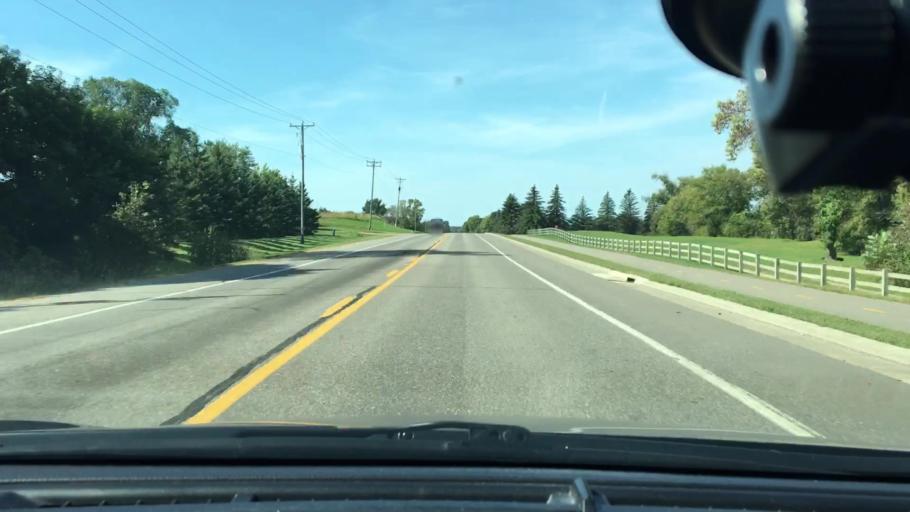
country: US
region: Minnesota
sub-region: Wright County
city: Hanover
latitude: 45.1525
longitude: -93.6467
